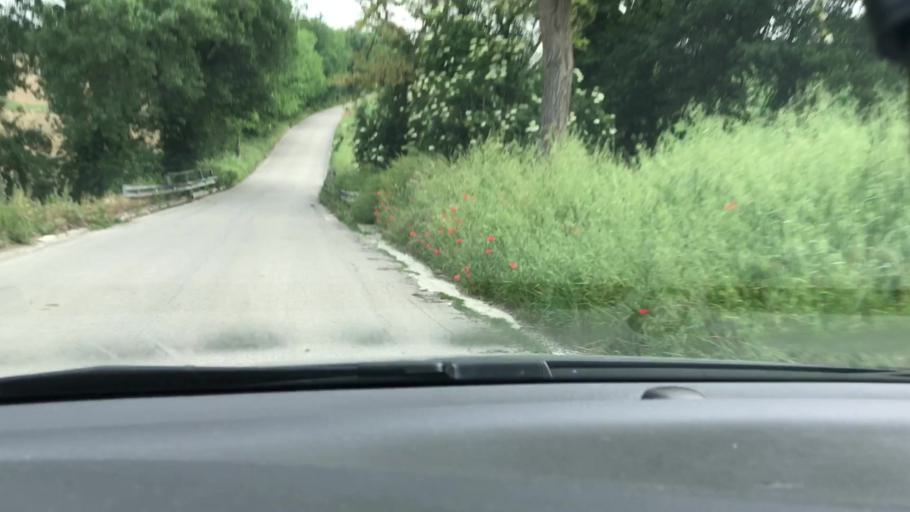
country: IT
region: The Marches
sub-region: Provincia di Macerata
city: Macerata
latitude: 43.2729
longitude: 13.4499
